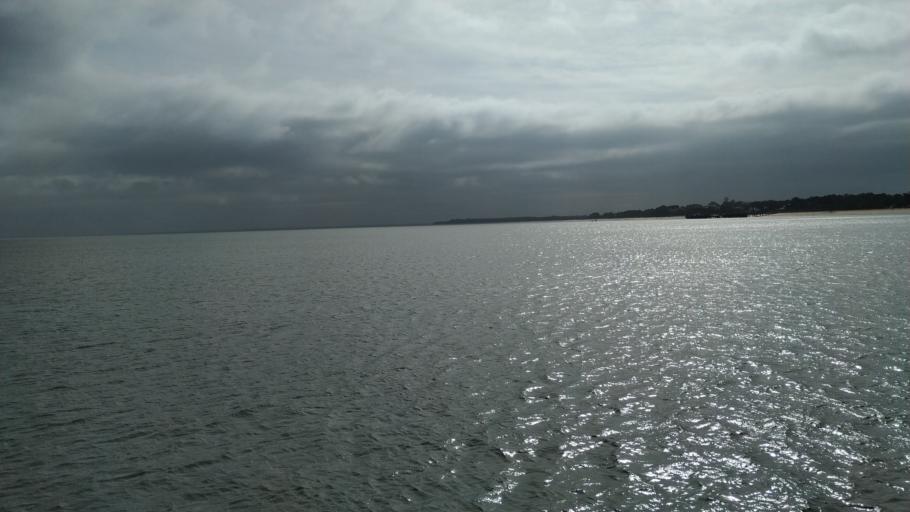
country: PT
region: Setubal
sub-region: Setubal
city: Setubal
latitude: 38.4750
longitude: -8.8673
